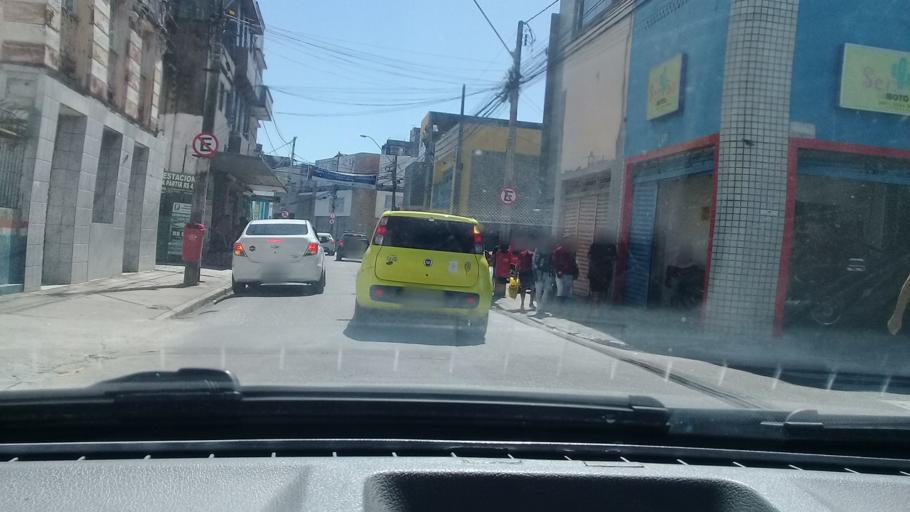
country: BR
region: Pernambuco
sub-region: Recife
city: Recife
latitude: -8.0693
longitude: -34.8828
